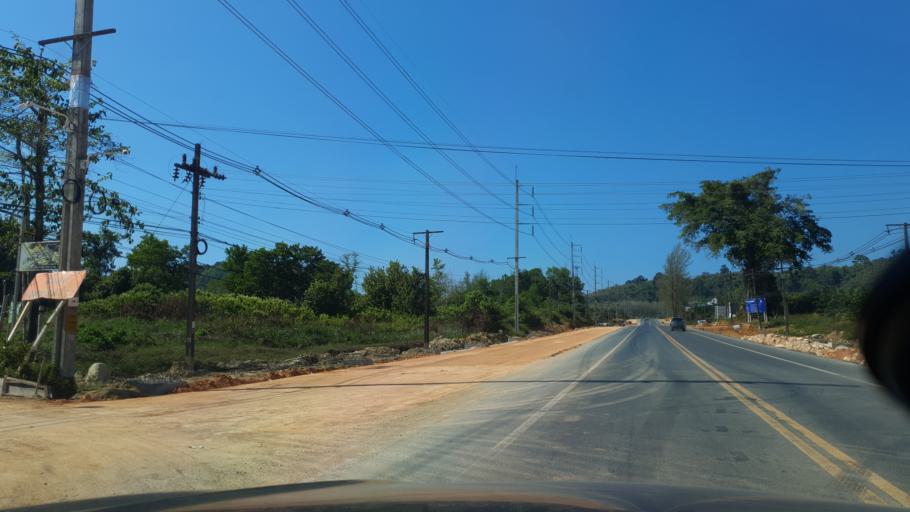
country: TH
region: Phangnga
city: Ban Khao Lak
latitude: 8.6014
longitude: 98.2534
